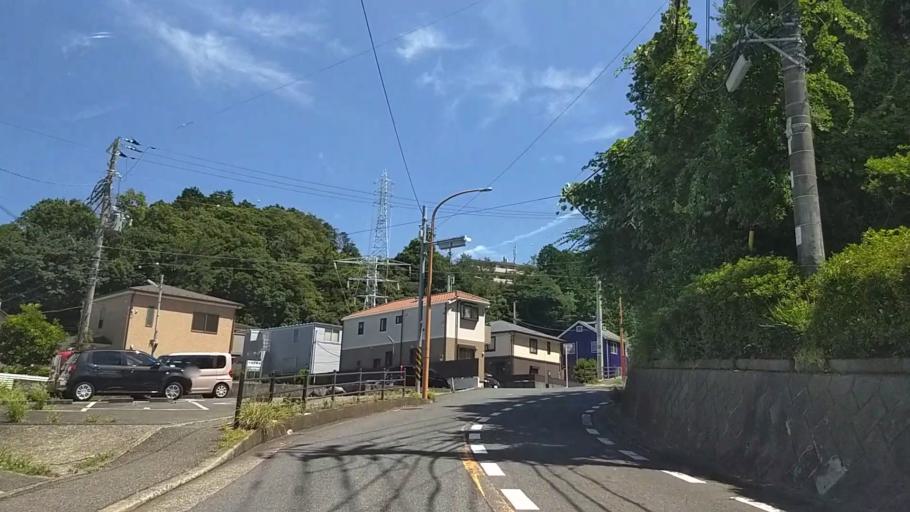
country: JP
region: Kanagawa
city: Zushi
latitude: 35.2958
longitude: 139.5906
